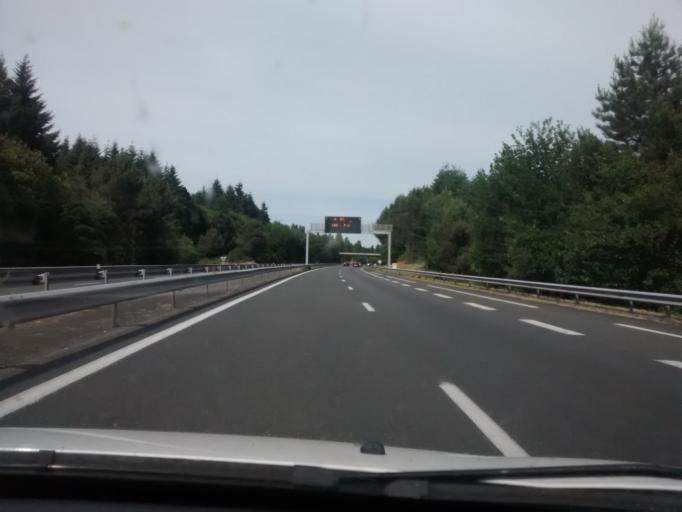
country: FR
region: Pays de la Loire
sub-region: Departement de la Sarthe
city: Pruille-le-Chetif
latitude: 48.0069
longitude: 0.0997
